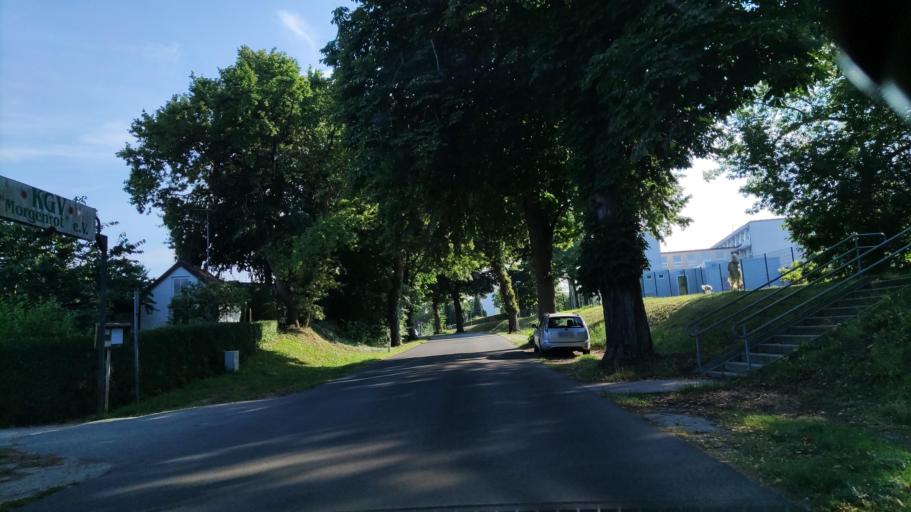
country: DE
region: Mecklenburg-Vorpommern
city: Boizenburg
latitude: 53.3833
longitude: 10.7328
